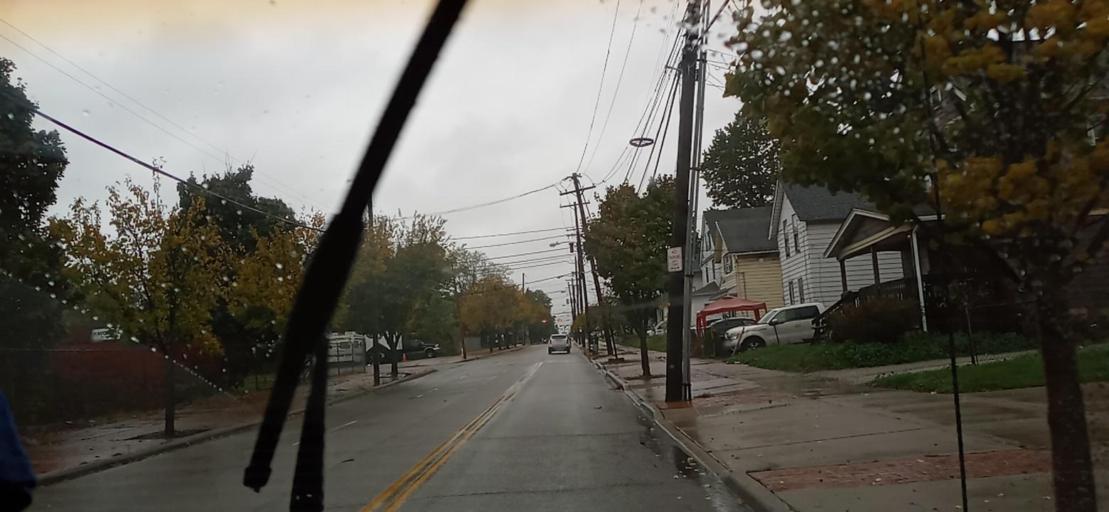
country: US
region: Ohio
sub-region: Summit County
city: Akron
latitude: 41.0754
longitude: -81.4991
